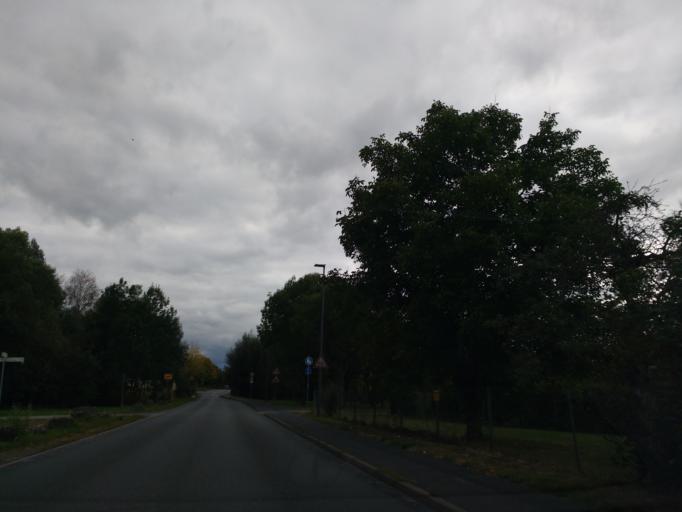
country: DE
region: Hesse
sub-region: Regierungsbezirk Kassel
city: Lohfelden
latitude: 51.2892
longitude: 9.5363
